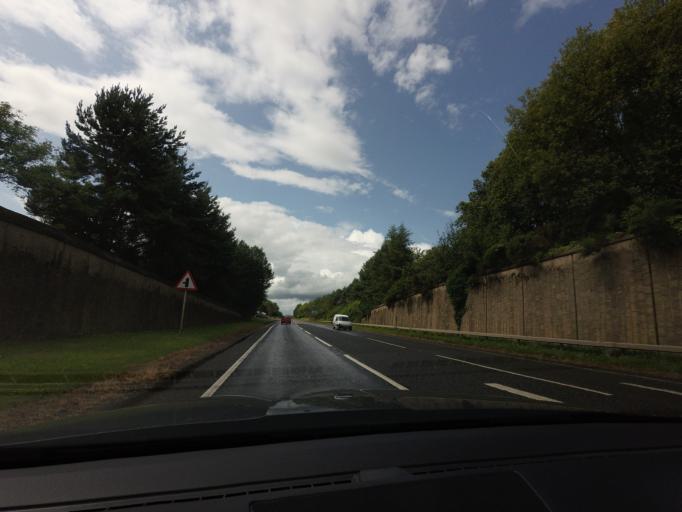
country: GB
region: Scotland
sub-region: Moray
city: Lhanbryd
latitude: 57.6335
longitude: -3.2228
